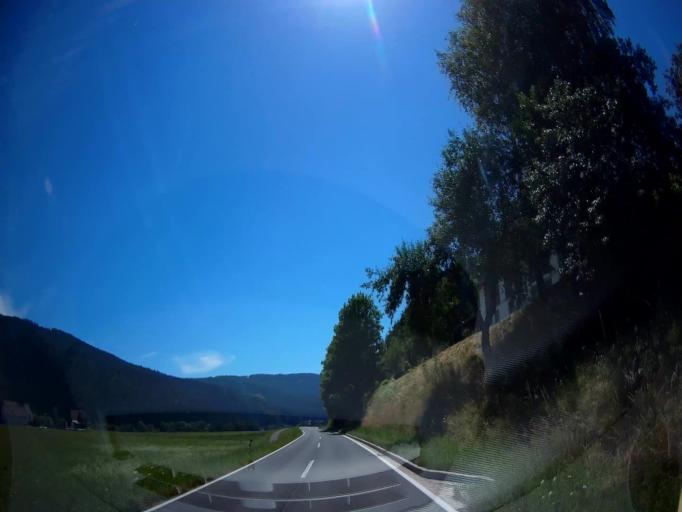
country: AT
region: Carinthia
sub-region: Politischer Bezirk Sankt Veit an der Glan
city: Gurk
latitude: 46.8562
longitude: 14.2166
